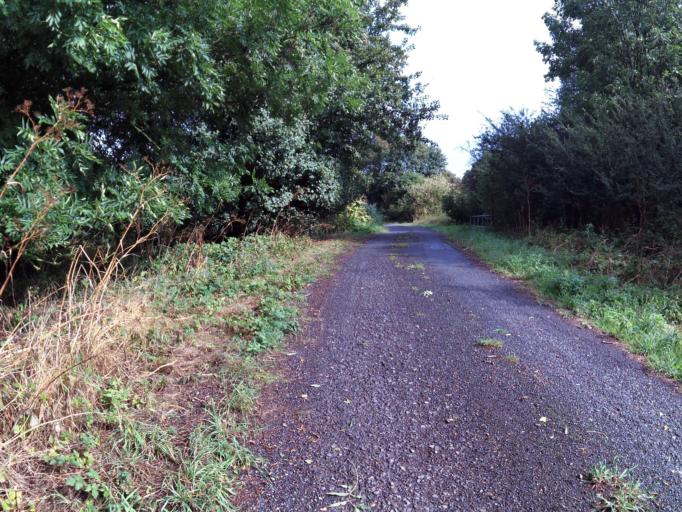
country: DE
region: Lower Saxony
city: Marklohe
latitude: 52.6624
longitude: 9.1799
